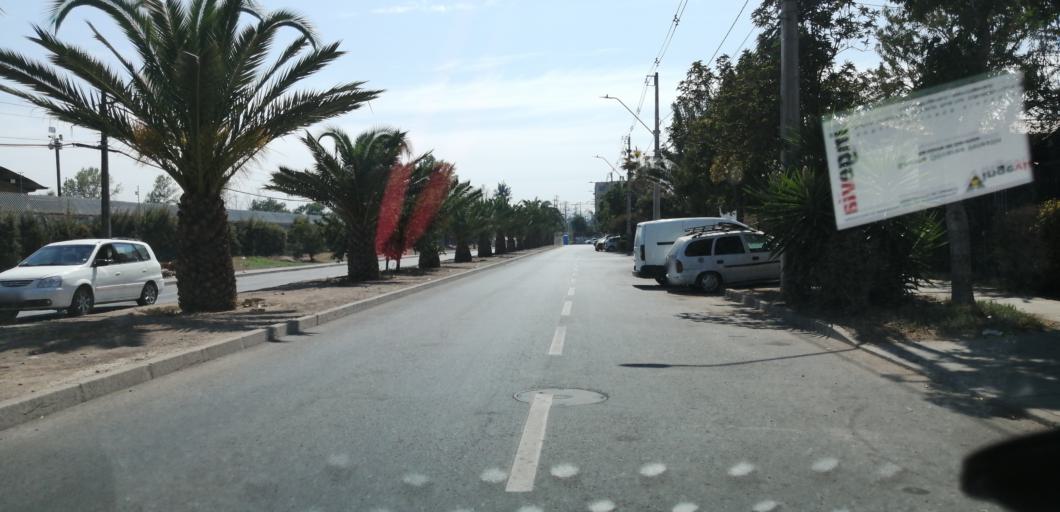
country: CL
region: Santiago Metropolitan
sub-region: Provincia de Santiago
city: Lo Prado
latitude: -33.4539
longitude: -70.7503
